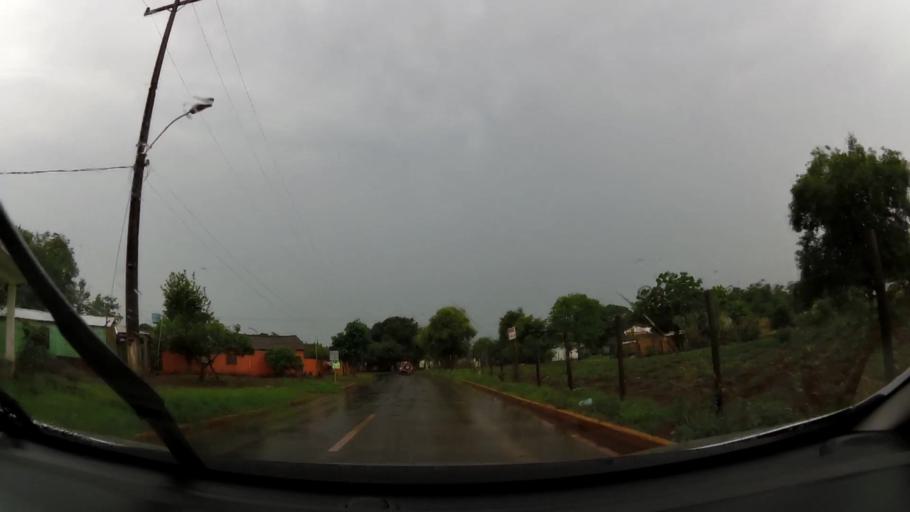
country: PY
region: Alto Parana
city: Presidente Franco
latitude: -25.5512
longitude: -54.6617
